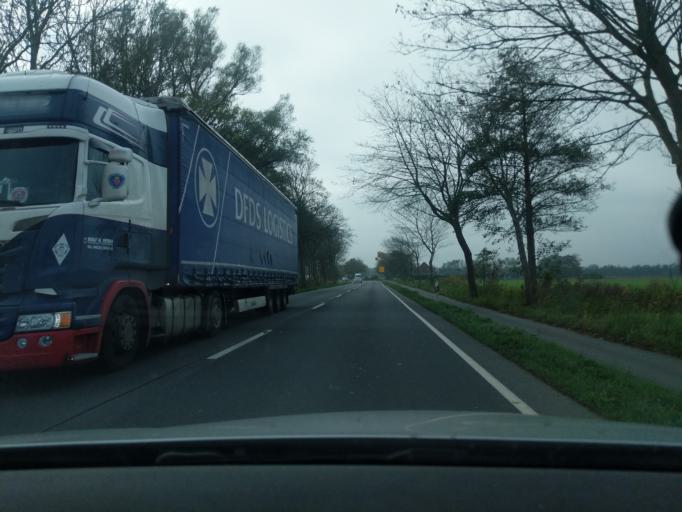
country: DE
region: Lower Saxony
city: Otterndorf
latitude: 53.8163
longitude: 8.9263
